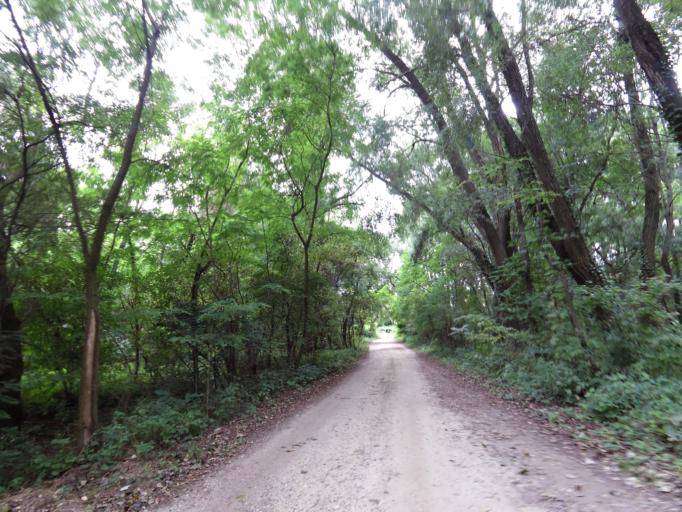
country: HU
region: Veszprem
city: Tapolca
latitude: 46.8368
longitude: 17.3685
